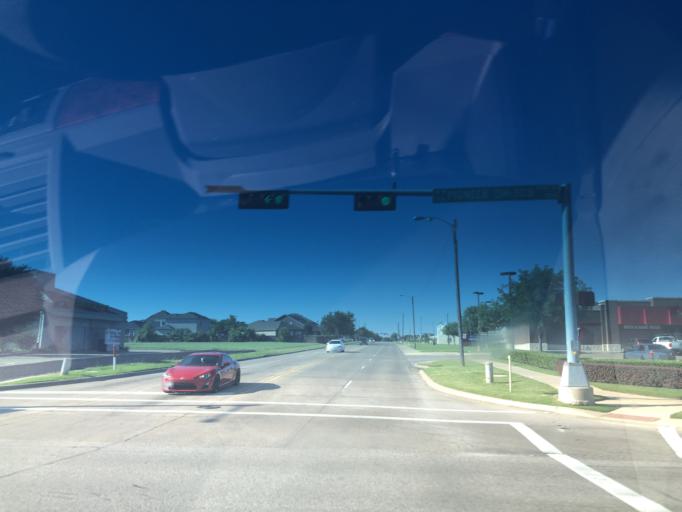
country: US
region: Texas
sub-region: Dallas County
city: Grand Prairie
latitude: 32.7096
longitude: -97.0198
